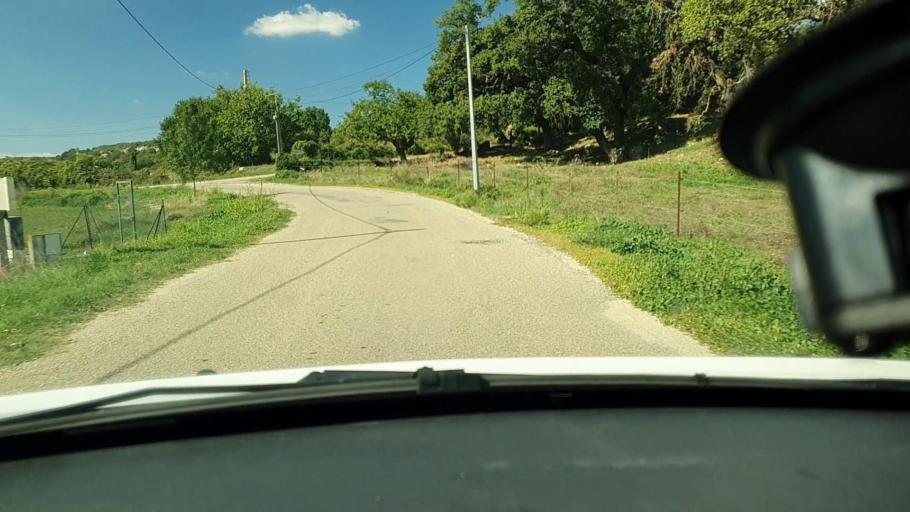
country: FR
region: Languedoc-Roussillon
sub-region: Departement du Gard
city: Goudargues
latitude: 44.1733
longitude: 4.3837
